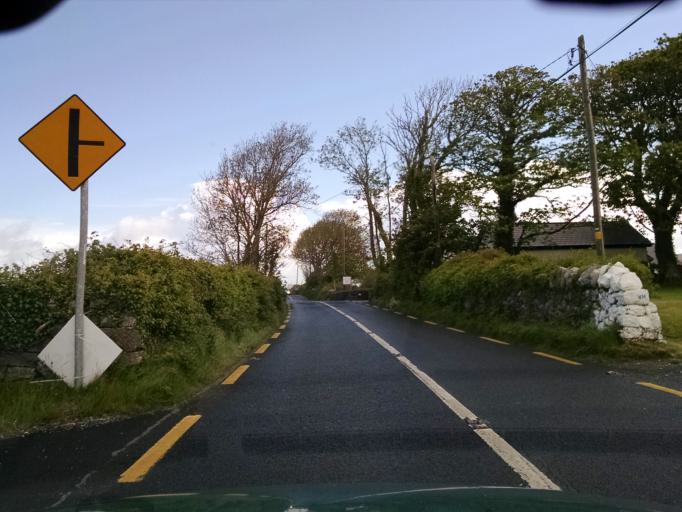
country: IE
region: Connaught
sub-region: County Galway
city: Bearna
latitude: 53.1016
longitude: -9.1629
